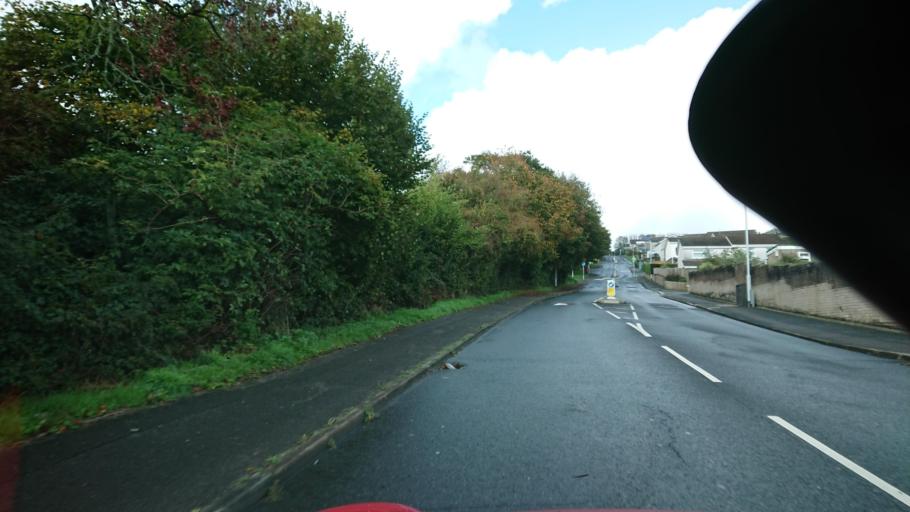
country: GB
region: England
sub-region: Plymouth
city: Plymouth
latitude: 50.3992
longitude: -4.1261
